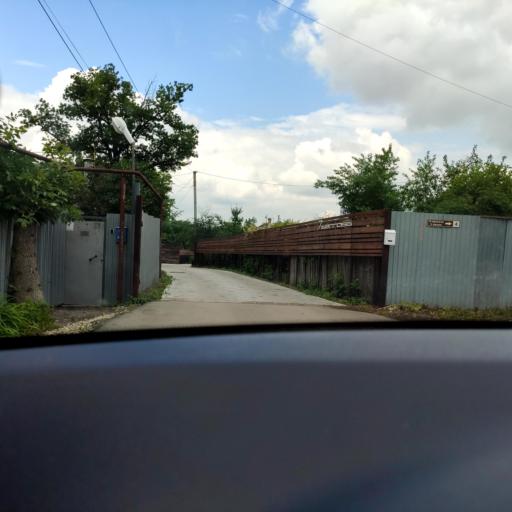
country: RU
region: Samara
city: Samara
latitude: 53.2735
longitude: 50.1873
